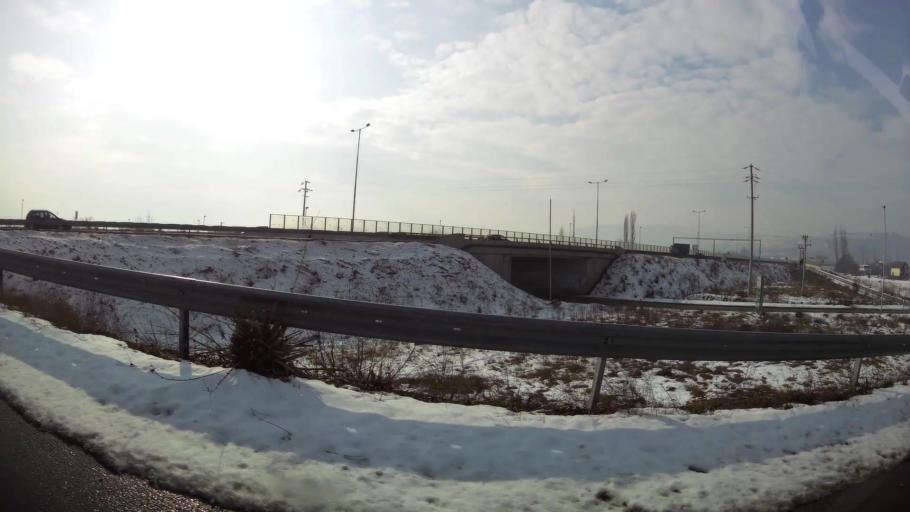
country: MK
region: Cucer-Sandevo
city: Chucher - Sandevo
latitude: 42.0536
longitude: 21.3648
